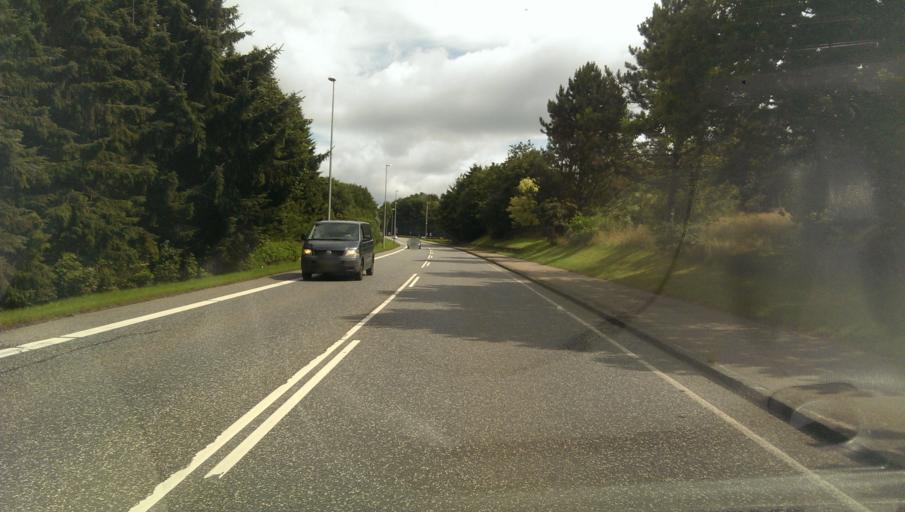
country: DK
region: South Denmark
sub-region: Vejle Kommune
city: Give
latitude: 55.8477
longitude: 9.2362
